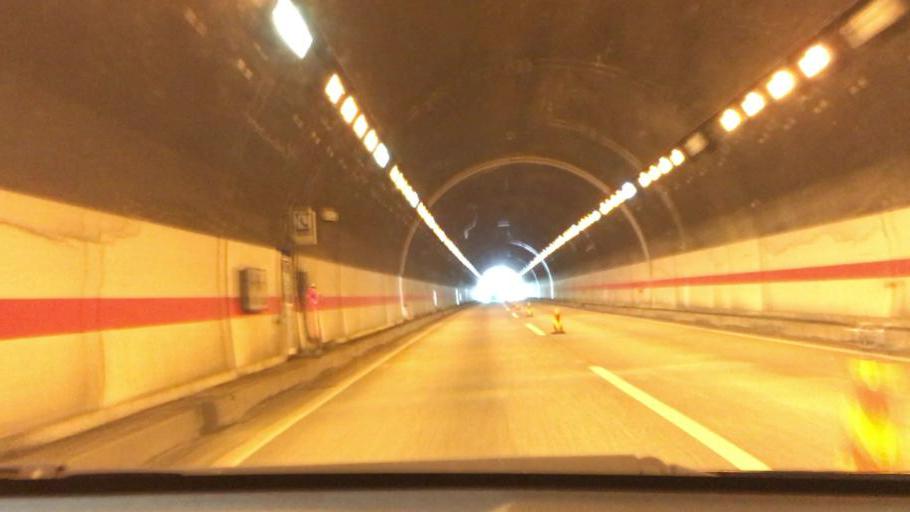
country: JP
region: Yamaguchi
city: Tokuyama
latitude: 34.0540
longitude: 131.8413
